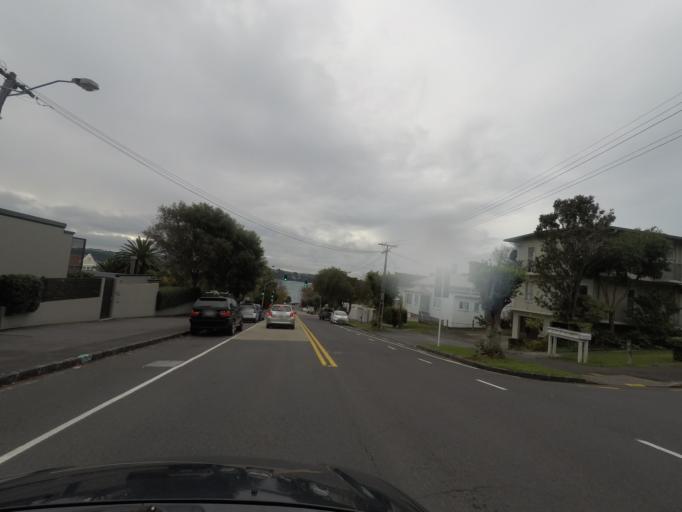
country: NZ
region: Auckland
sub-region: Auckland
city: Auckland
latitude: -36.8431
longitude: 174.7399
